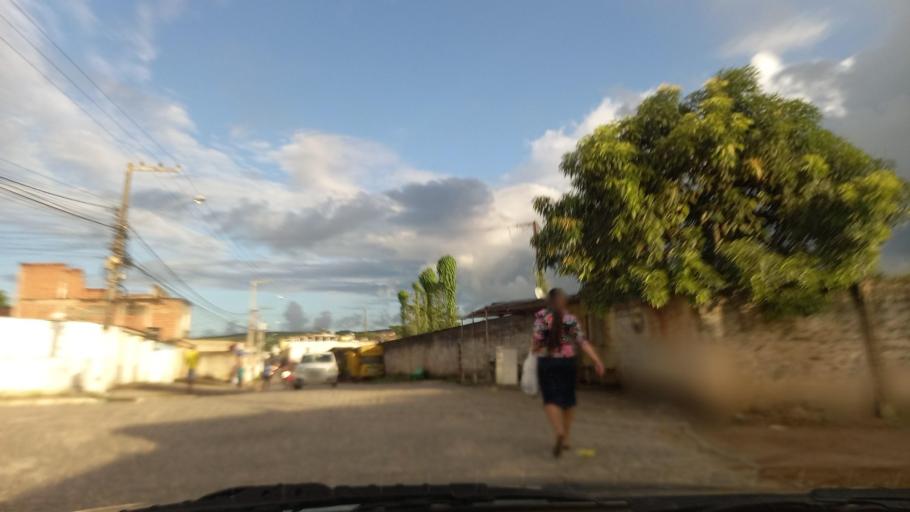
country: BR
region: Pernambuco
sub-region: Palmares
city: Palmares
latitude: -8.6806
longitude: -35.5958
